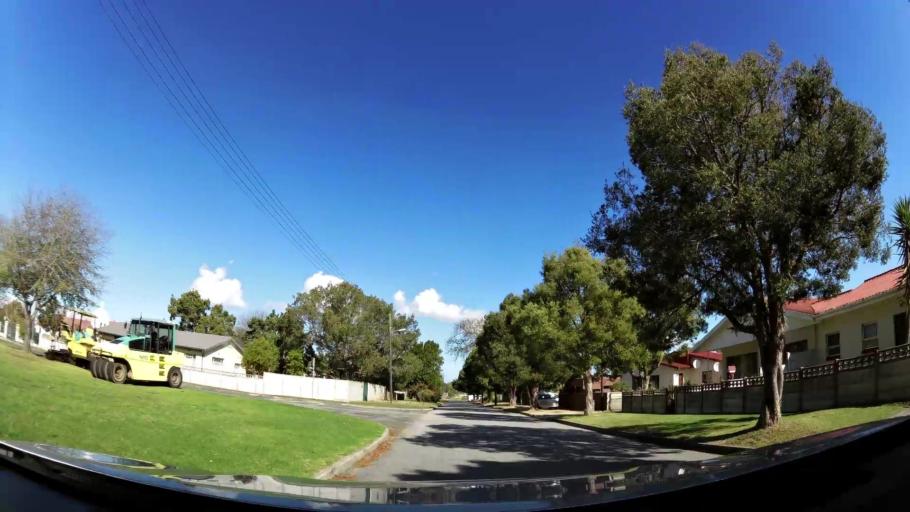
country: ZA
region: Western Cape
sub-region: Eden District Municipality
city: George
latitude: -33.9495
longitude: 22.4741
